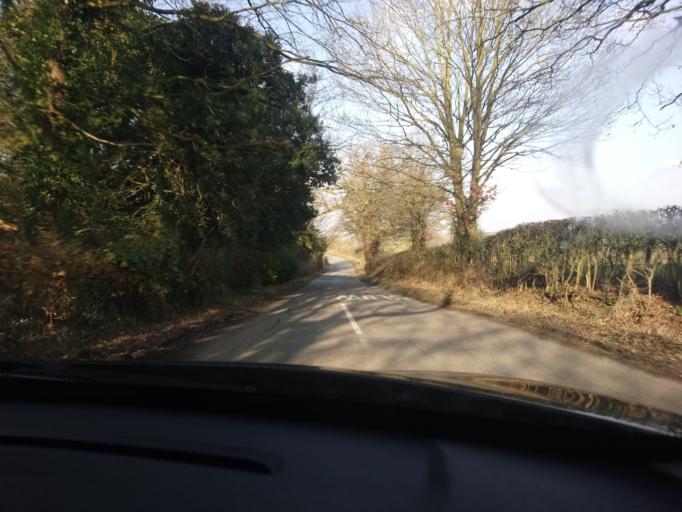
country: GB
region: England
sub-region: Shropshire
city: Bicton
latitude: 52.7529
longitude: -2.7791
